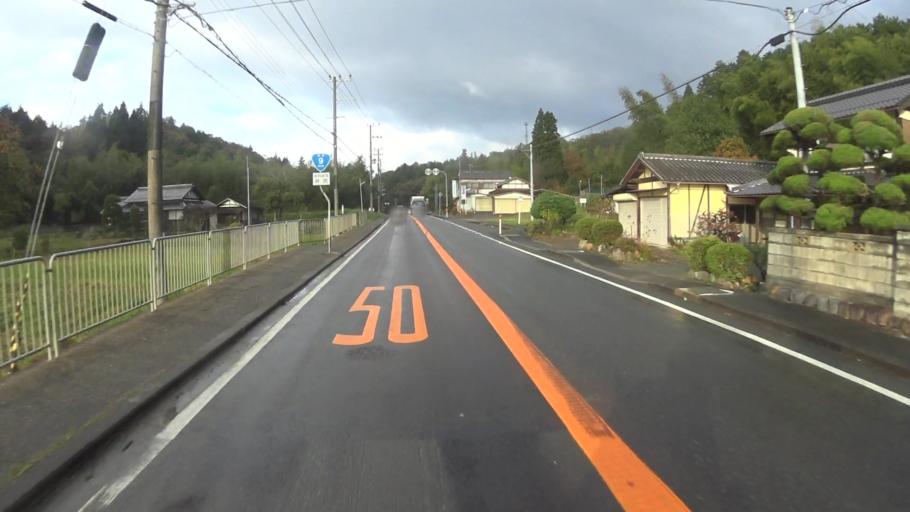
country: JP
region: Kyoto
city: Ayabe
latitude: 35.1792
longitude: 135.3589
